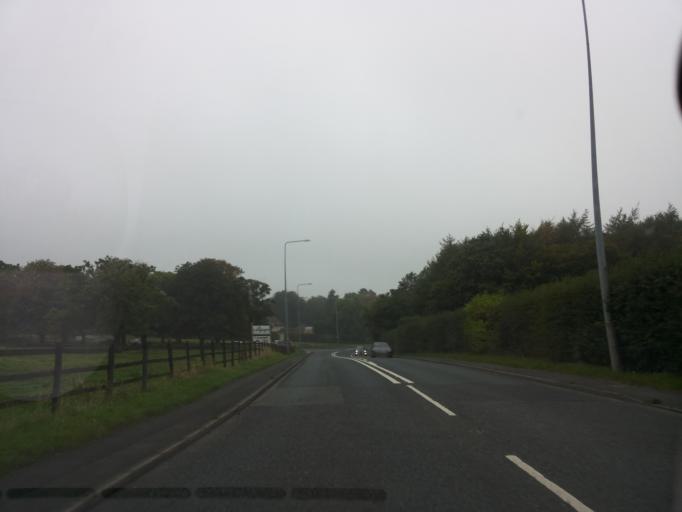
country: GB
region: England
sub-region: Lancashire
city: Langho
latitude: 53.8052
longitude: -2.4665
